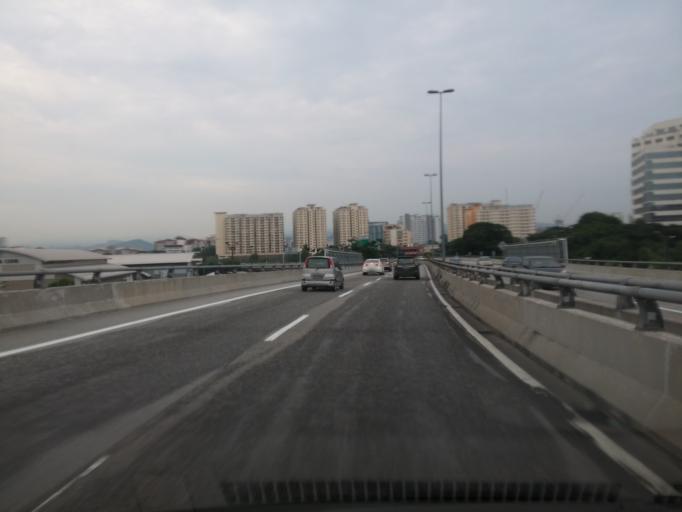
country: MY
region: Kuala Lumpur
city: Kuala Lumpur
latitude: 3.1233
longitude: 101.7165
